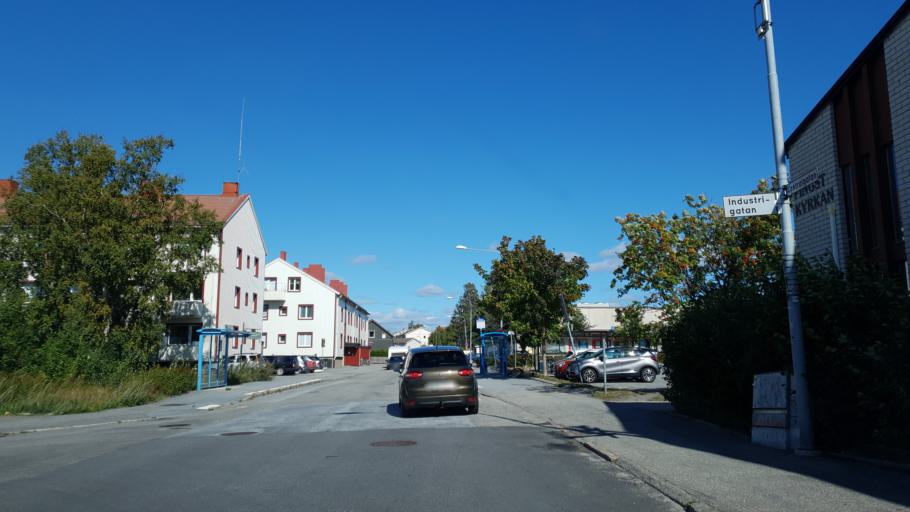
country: SE
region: Vaesterbotten
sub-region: Umea Kommun
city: Holmsund
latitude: 63.7075
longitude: 20.3640
